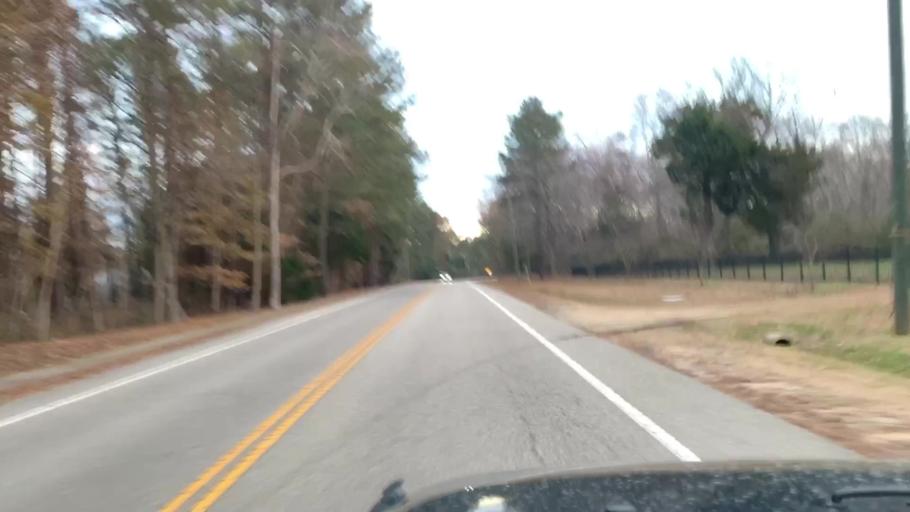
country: US
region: Virginia
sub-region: City of Williamsburg
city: Williamsburg
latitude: 37.2558
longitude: -76.7104
